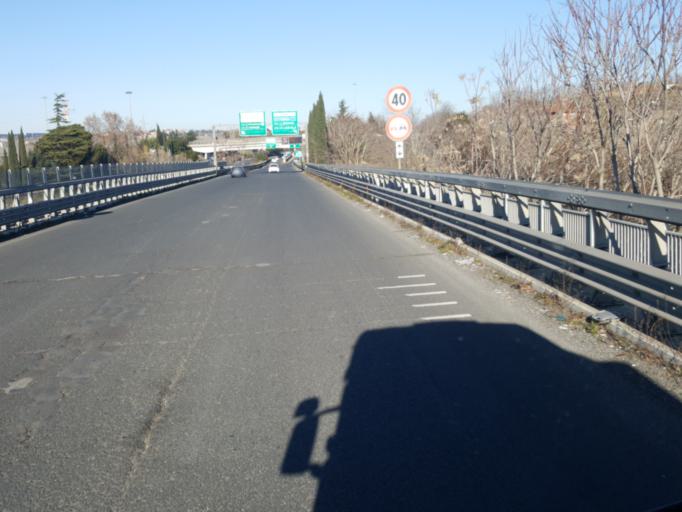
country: IT
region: Latium
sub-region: Citta metropolitana di Roma Capitale
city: Vitinia
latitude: 41.8035
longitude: 12.4193
